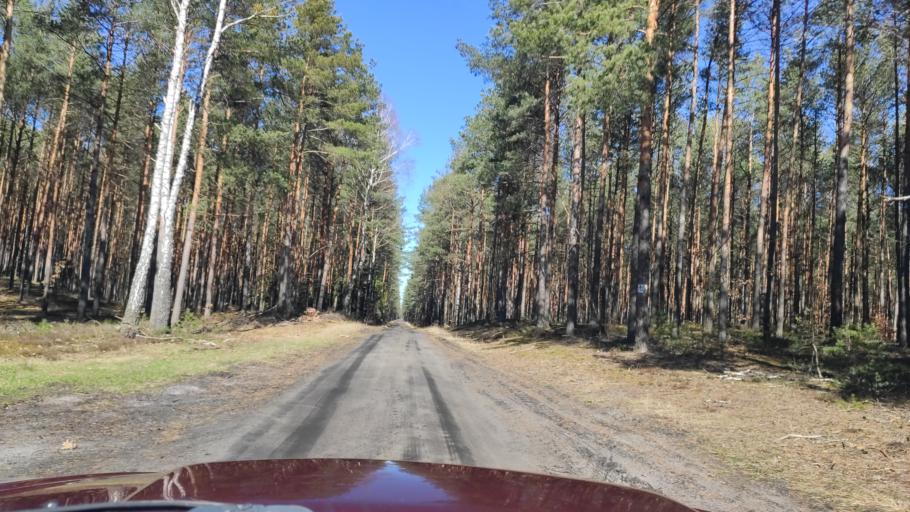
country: PL
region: Masovian Voivodeship
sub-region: Powiat zwolenski
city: Zwolen
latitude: 51.4156
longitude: 21.5546
